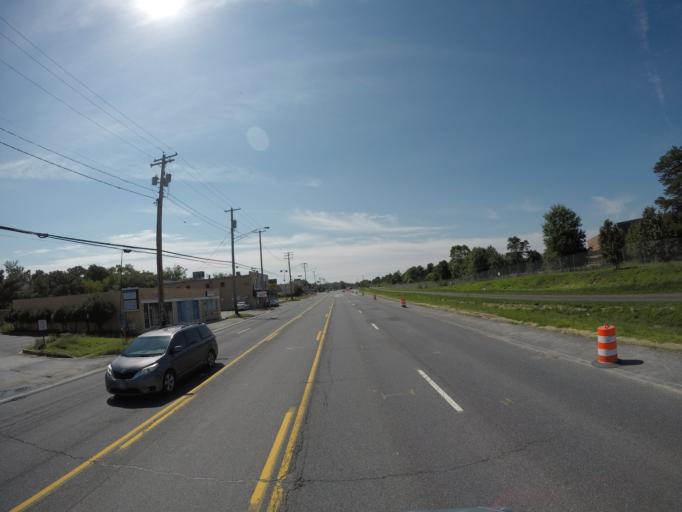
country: US
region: Maryland
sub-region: Anne Arundel County
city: Fort Meade
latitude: 39.1082
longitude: -76.7237
